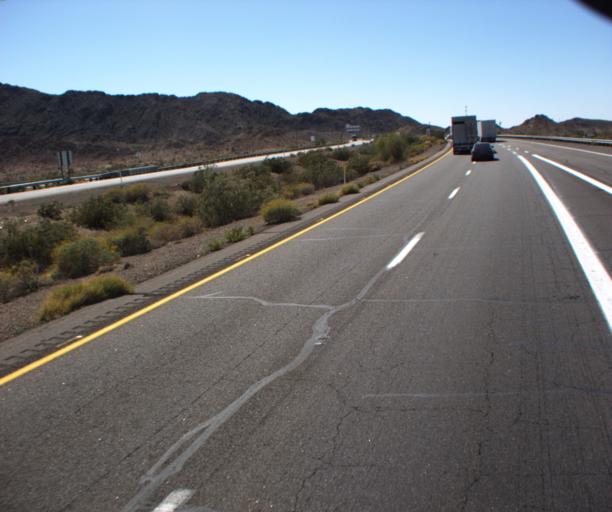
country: US
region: Arizona
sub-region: Yuma County
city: Wellton
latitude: 32.7294
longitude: -113.7335
